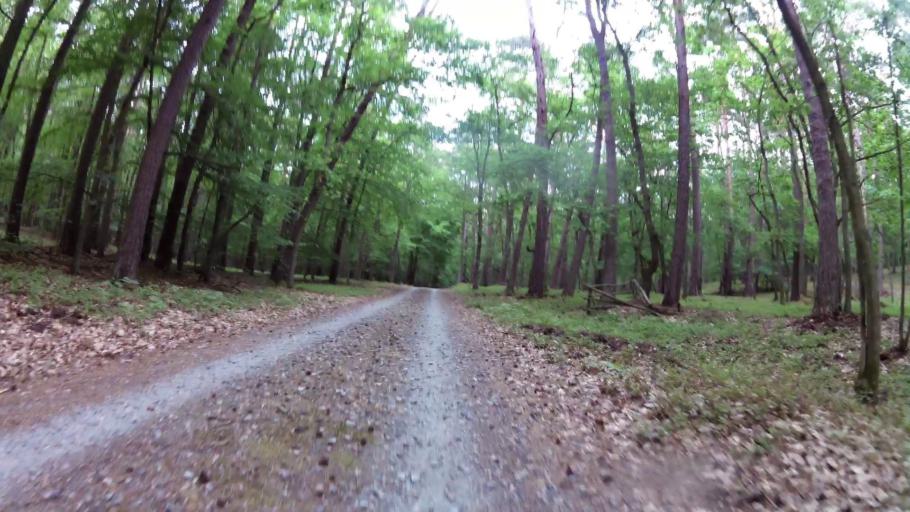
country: PL
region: West Pomeranian Voivodeship
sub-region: Powiat kamienski
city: Miedzyzdroje
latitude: 53.9375
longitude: 14.4935
